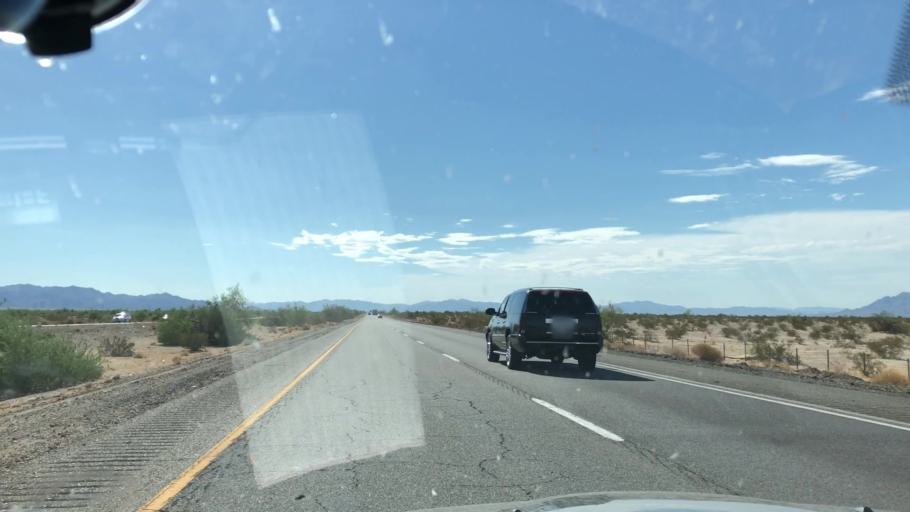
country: US
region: California
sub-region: Riverside County
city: Mesa Verde
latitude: 33.6521
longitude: -115.1403
